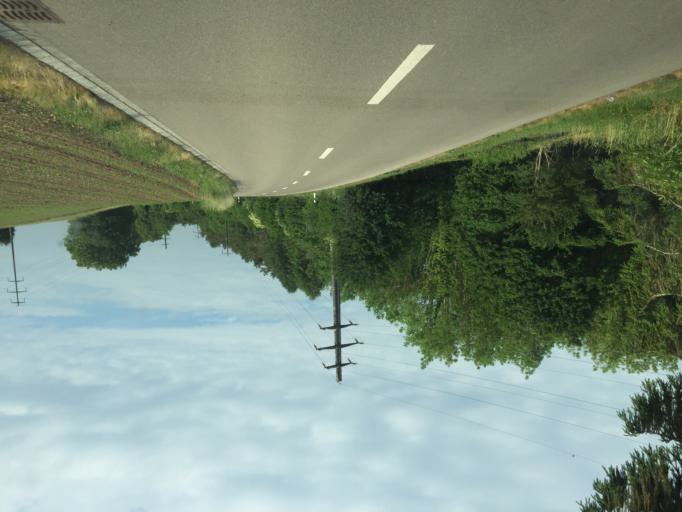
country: DE
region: Baden-Wuerttemberg
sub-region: Freiburg Region
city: Lottstetten
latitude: 47.6280
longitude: 8.6003
